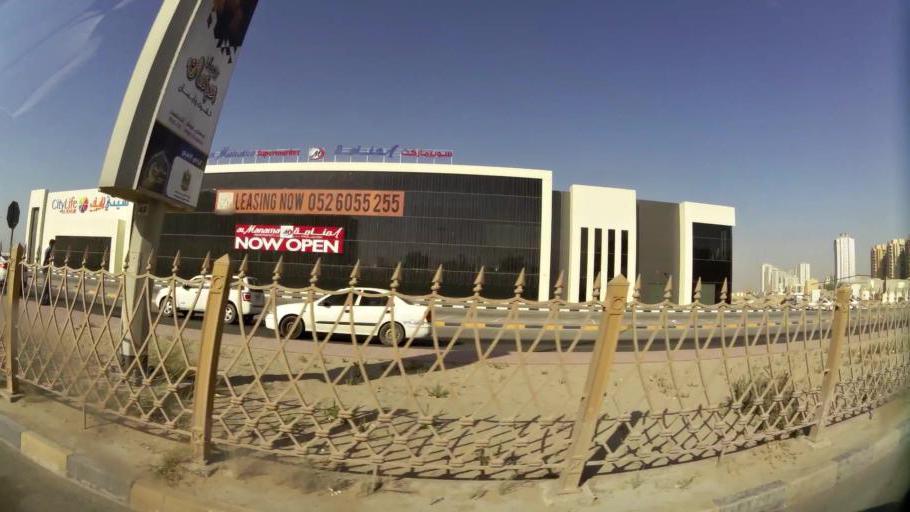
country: AE
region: Ajman
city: Ajman
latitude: 25.3981
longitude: 55.4537
